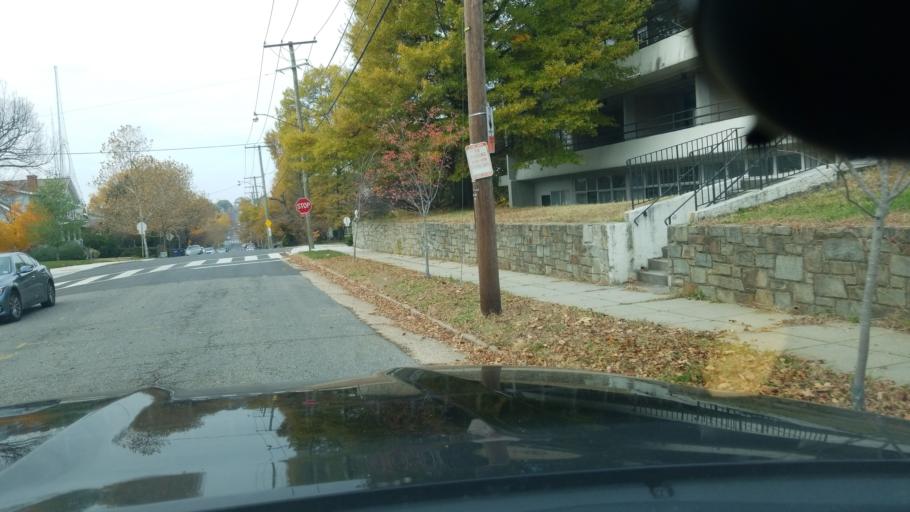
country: US
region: Maryland
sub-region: Montgomery County
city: Takoma Park
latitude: 38.9650
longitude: -77.0139
